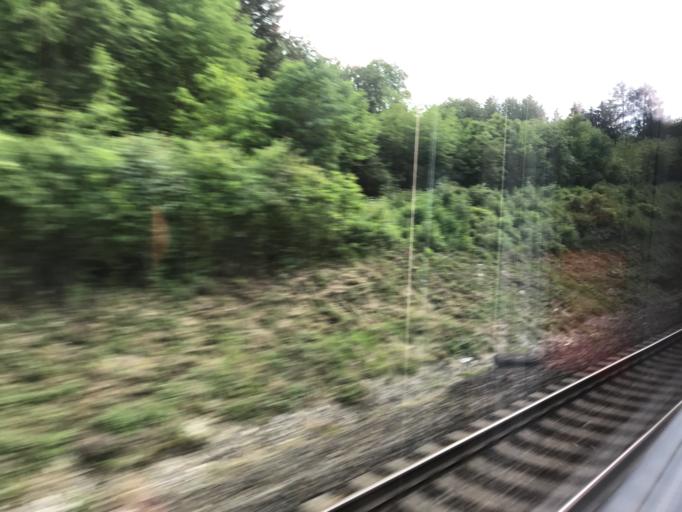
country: DE
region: Baden-Wuerttemberg
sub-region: Tuebingen Region
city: Westerstetten
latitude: 48.5020
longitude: 9.9542
